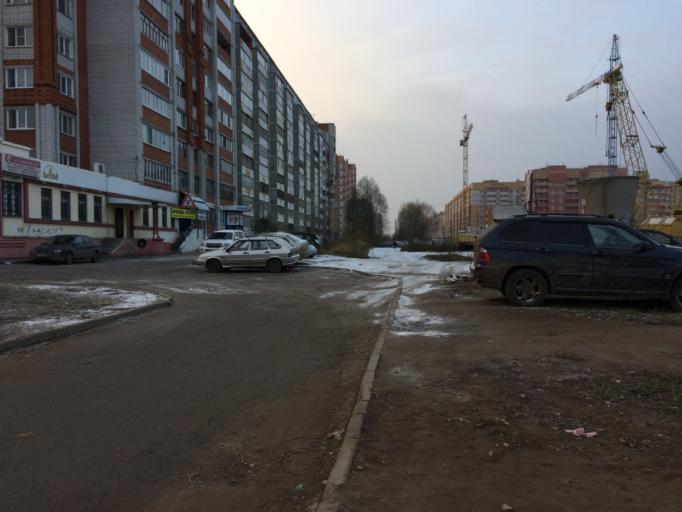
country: RU
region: Mariy-El
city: Yoshkar-Ola
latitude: 56.6376
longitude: 47.9336
